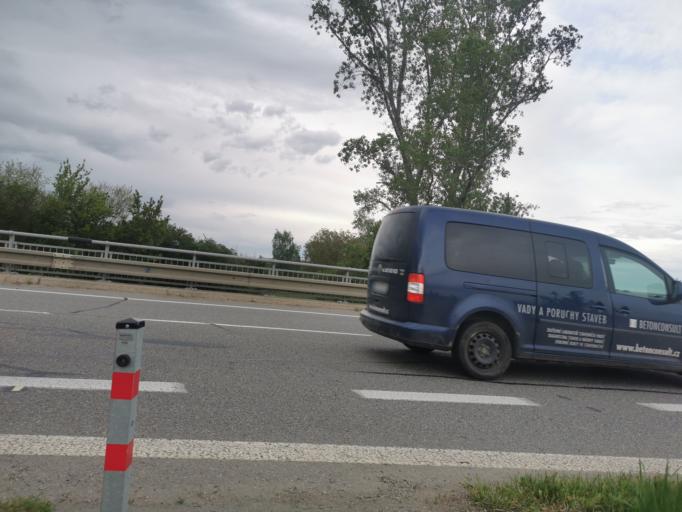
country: CZ
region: South Moravian
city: Sudomerice
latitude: 48.8763
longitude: 17.2393
